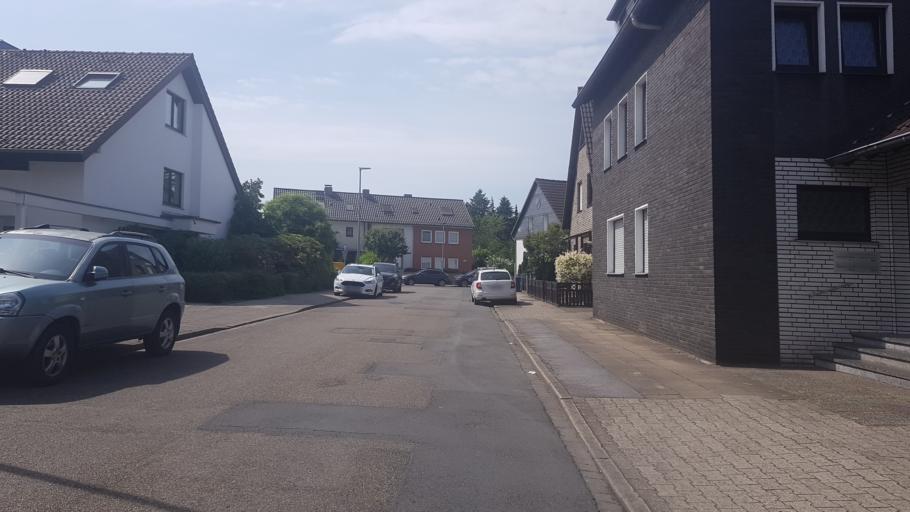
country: DE
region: North Rhine-Westphalia
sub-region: Regierungsbezirk Dusseldorf
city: Oberhausen
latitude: 51.4630
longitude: 6.8692
